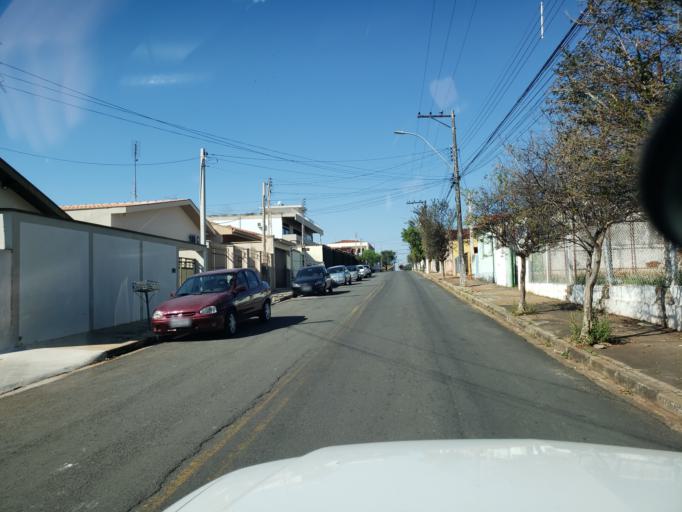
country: BR
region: Sao Paulo
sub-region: Itapira
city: Itapira
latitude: -22.4374
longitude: -46.8326
